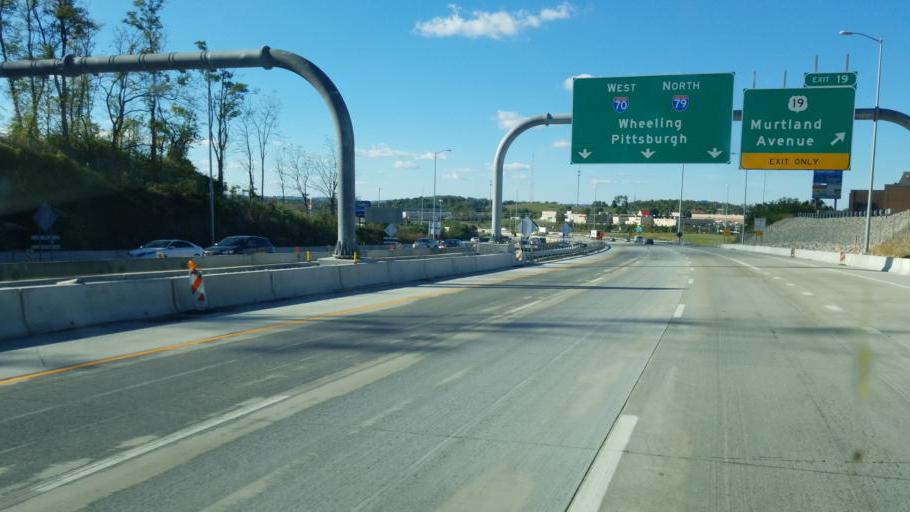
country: US
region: Pennsylvania
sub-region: Washington County
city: East Washington
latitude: 40.1809
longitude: -80.2242
